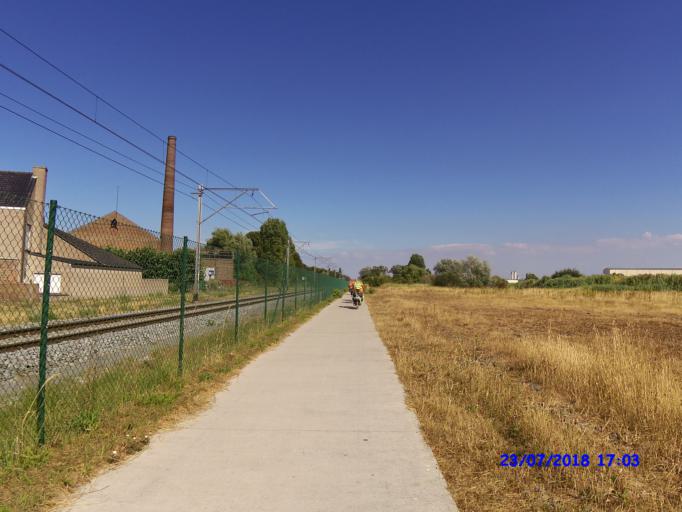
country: BE
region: Flanders
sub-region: Provincie West-Vlaanderen
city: Veurne
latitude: 51.0725
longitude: 2.6788
